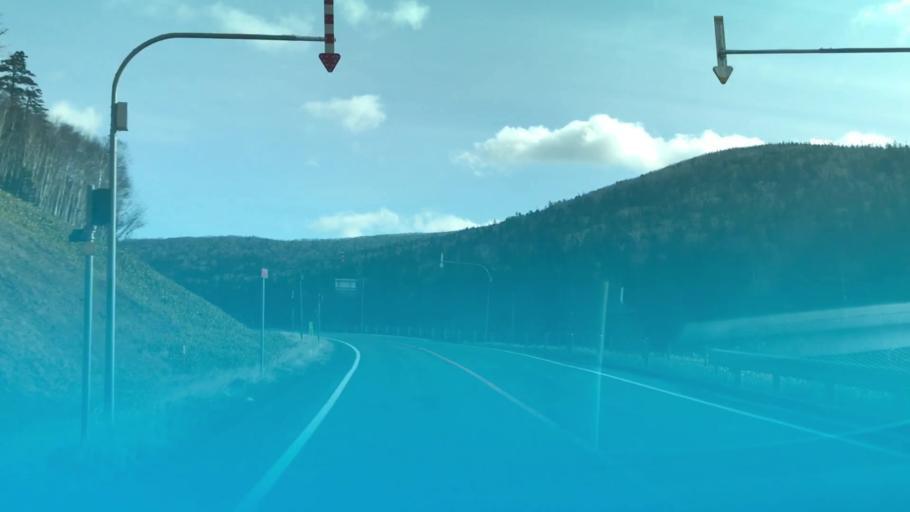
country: JP
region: Hokkaido
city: Otofuke
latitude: 42.9830
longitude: 142.7424
